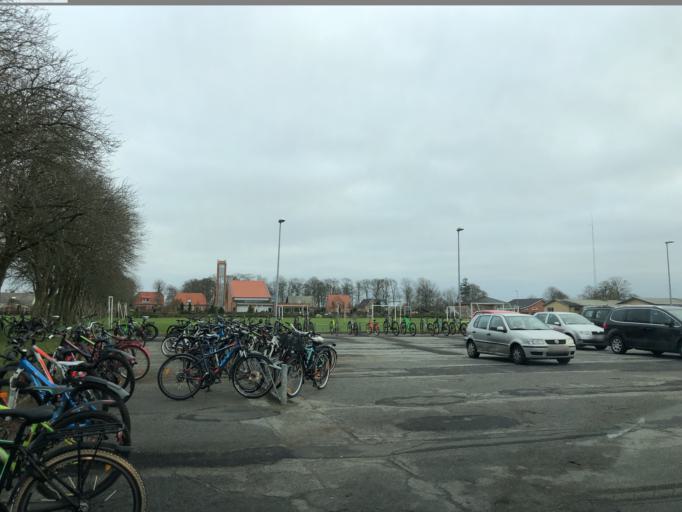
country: DK
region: Central Jutland
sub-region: Viborg Kommune
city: Stoholm
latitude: 56.4836
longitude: 9.1467
